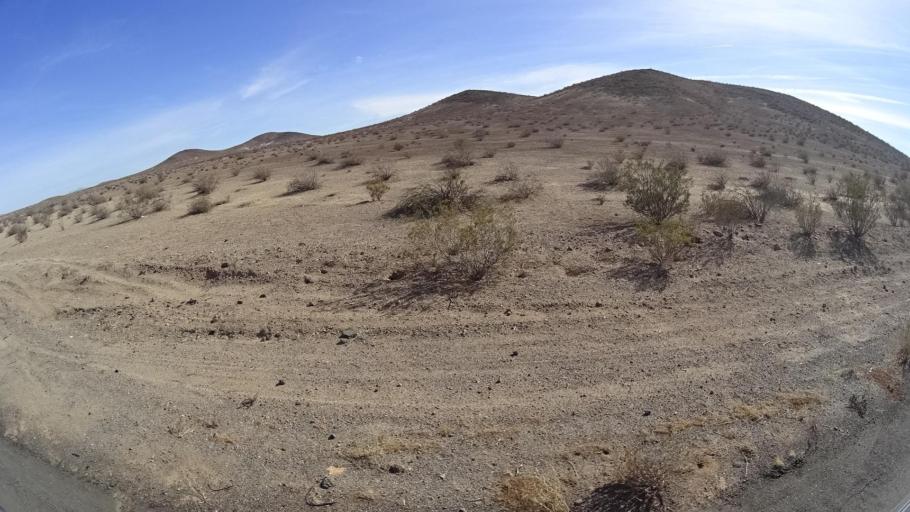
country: US
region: California
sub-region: Kern County
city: North Edwards
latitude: 35.0409
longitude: -117.8248
